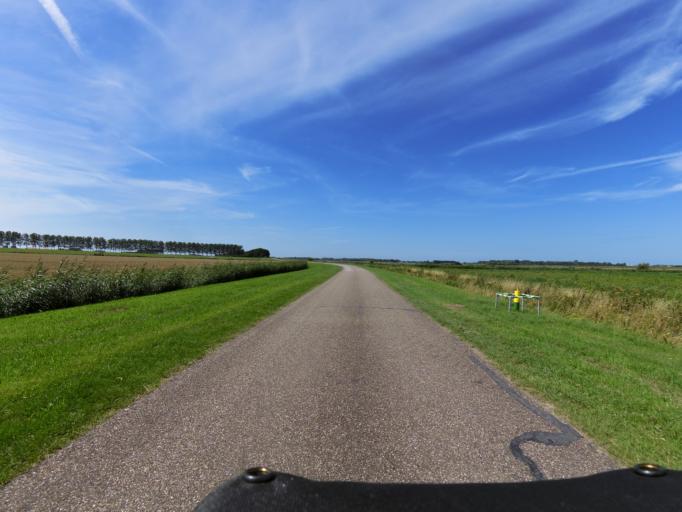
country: NL
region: South Holland
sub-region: Gemeente Goeree-Overflakkee
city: Dirksland
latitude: 51.8023
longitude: 4.0625
